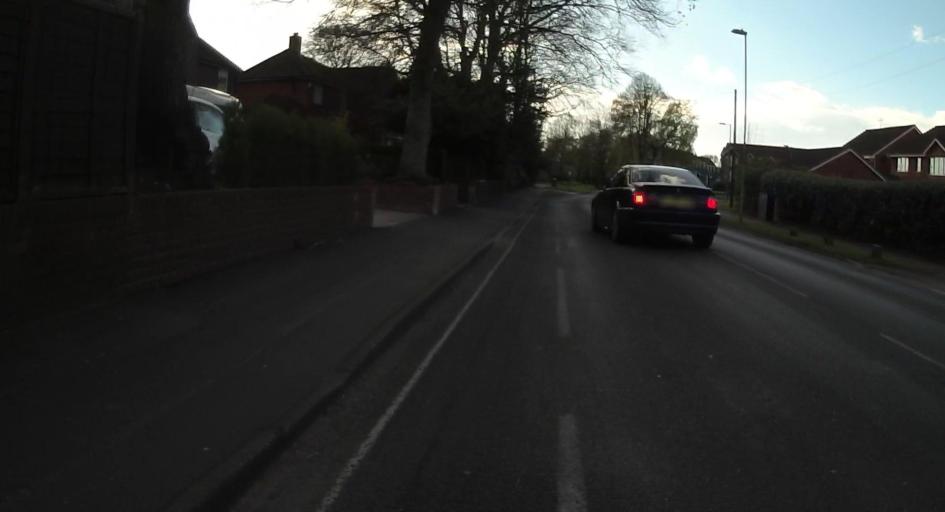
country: GB
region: England
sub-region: Hampshire
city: Farnborough
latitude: 51.3043
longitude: -0.7581
